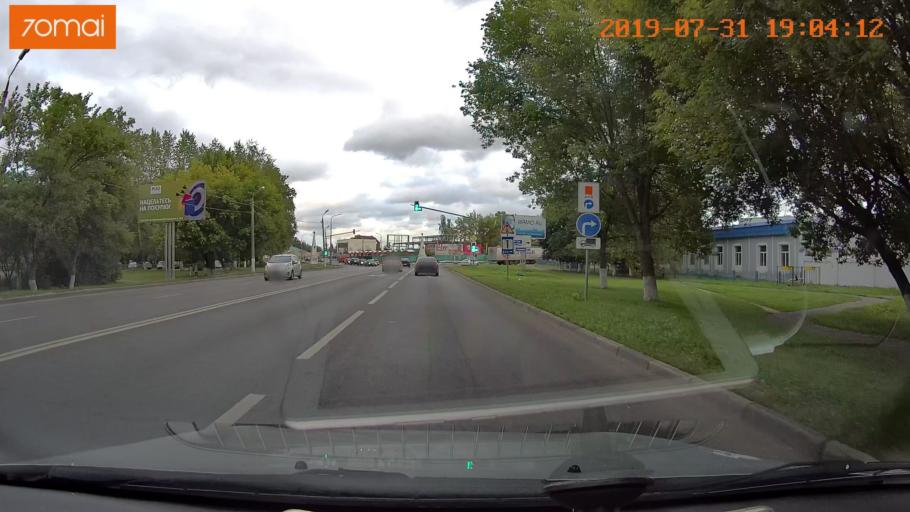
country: RU
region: Moskovskaya
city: Raduzhnyy
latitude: 55.1102
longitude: 38.7397
